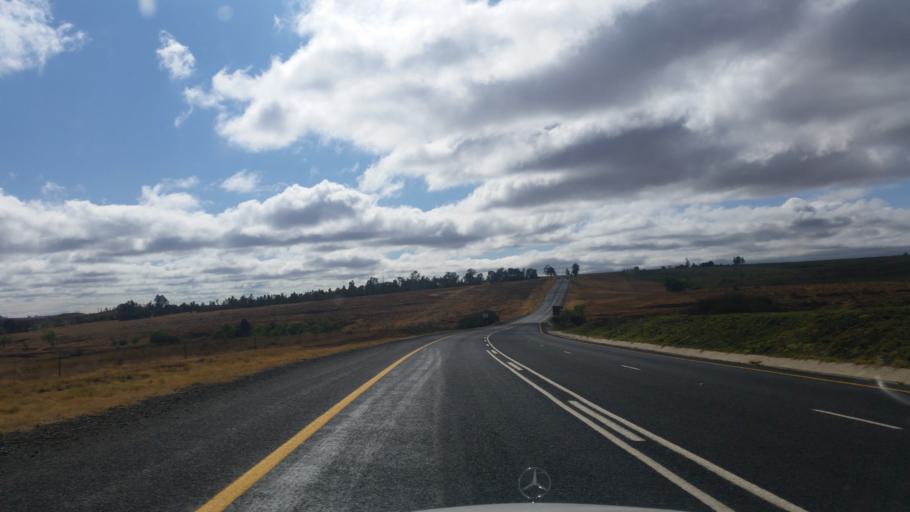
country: ZA
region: Orange Free State
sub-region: Thabo Mofutsanyana District Municipality
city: Phuthaditjhaba
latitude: -28.2959
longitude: 28.8023
